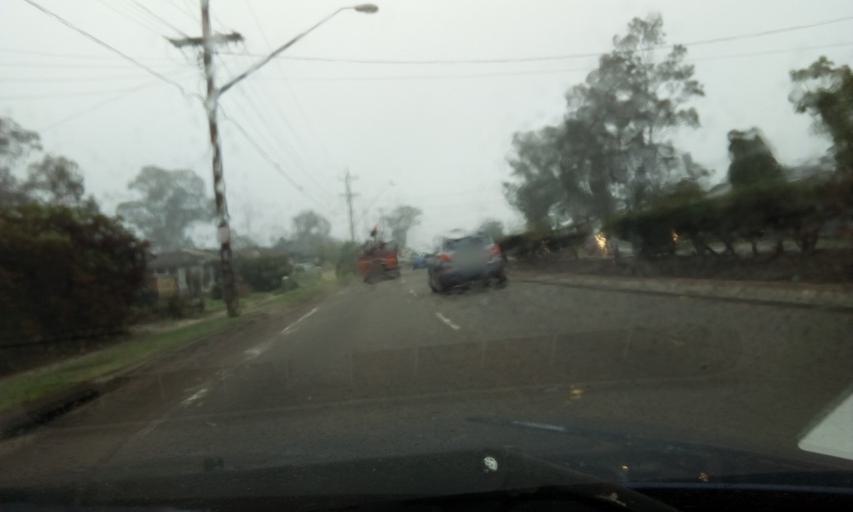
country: AU
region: New South Wales
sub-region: Penrith Municipality
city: Cambridge Park
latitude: -33.7455
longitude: 150.7146
